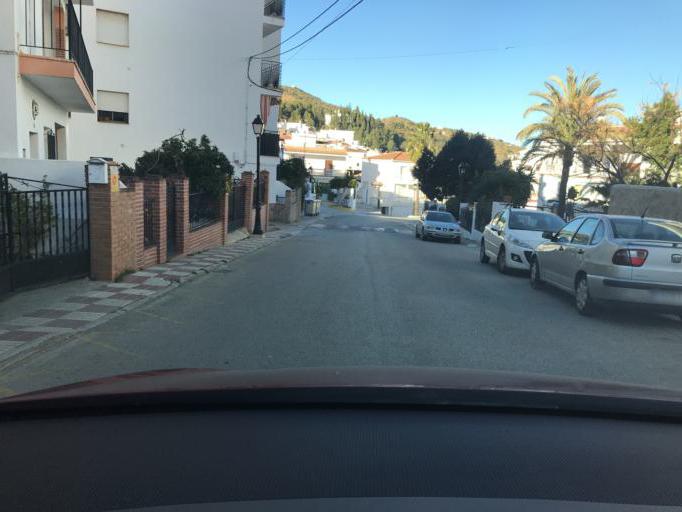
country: ES
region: Andalusia
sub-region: Provincia de Malaga
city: Tolox
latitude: 36.6854
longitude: -4.9046
